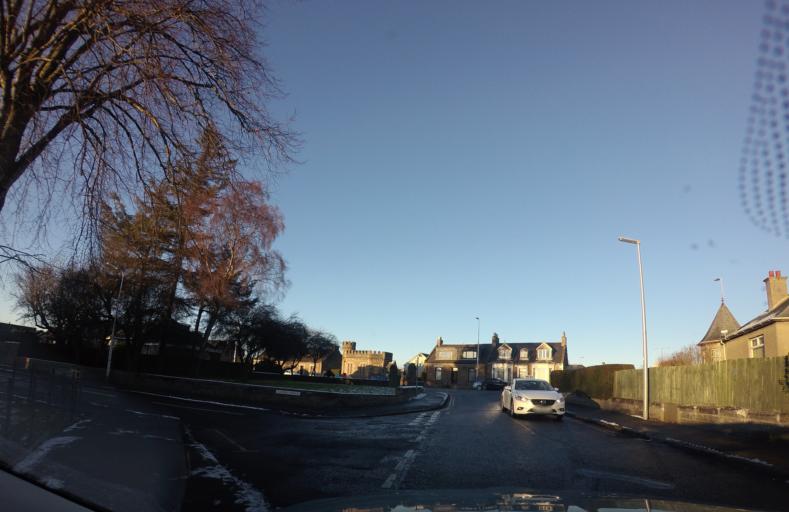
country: GB
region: Scotland
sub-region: Dundee City
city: Dundee
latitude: 56.4784
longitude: -2.9898
